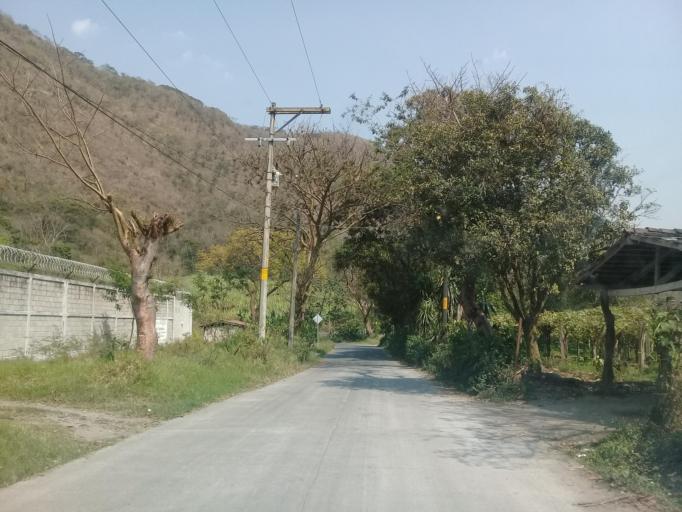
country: MX
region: Veracruz
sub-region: Ixtaczoquitlan
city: Campo Chico
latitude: 18.8337
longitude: -97.0177
